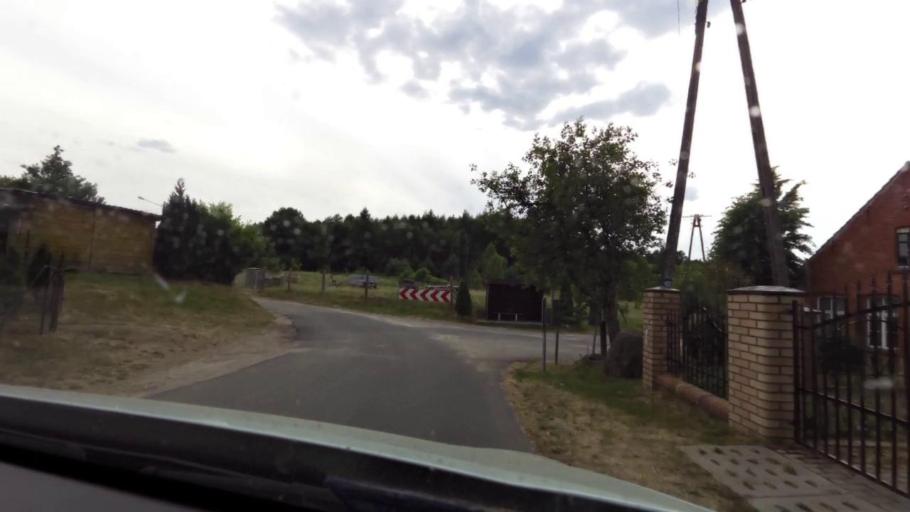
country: PL
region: Pomeranian Voivodeship
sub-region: Powiat bytowski
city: Trzebielino
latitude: 54.2592
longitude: 17.0089
